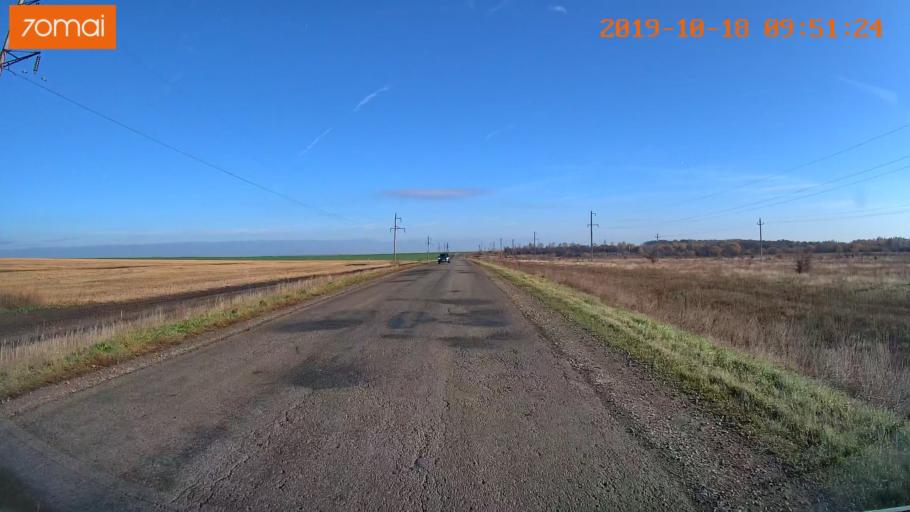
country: RU
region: Tula
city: Kazachka
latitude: 53.3402
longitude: 38.2920
